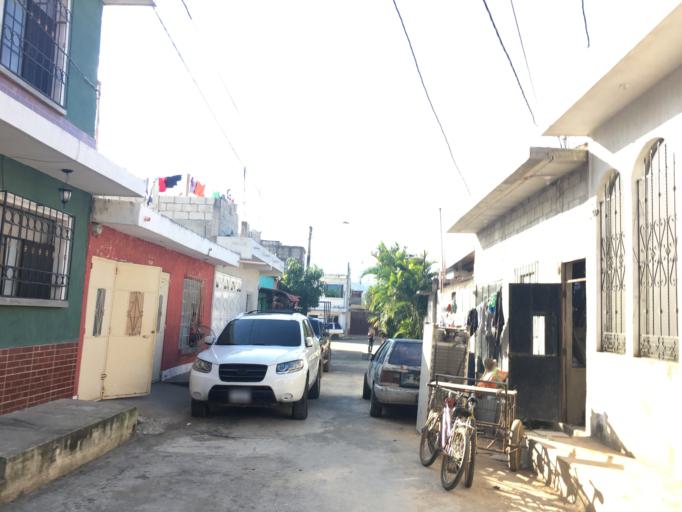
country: GT
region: Guatemala
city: Petapa
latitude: 14.4972
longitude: -90.5694
